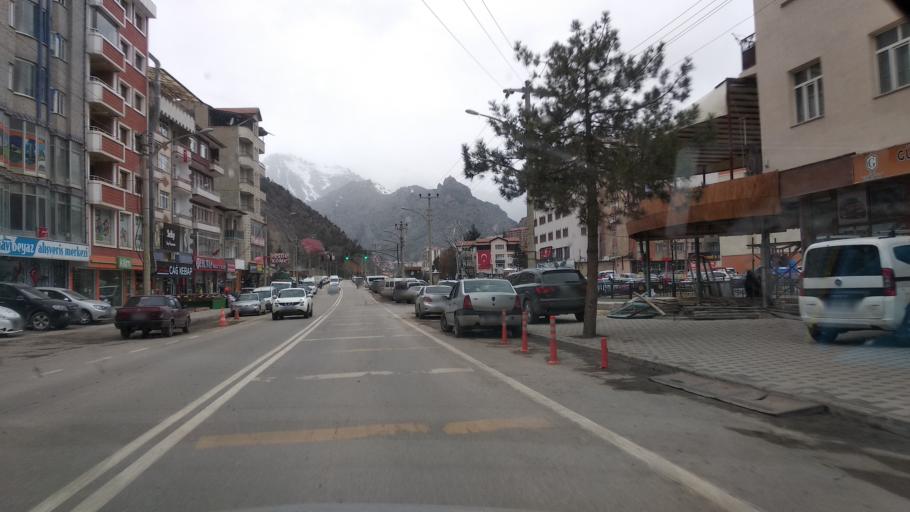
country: TR
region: Gumushane
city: Gumushkhane
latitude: 40.4576
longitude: 39.4801
